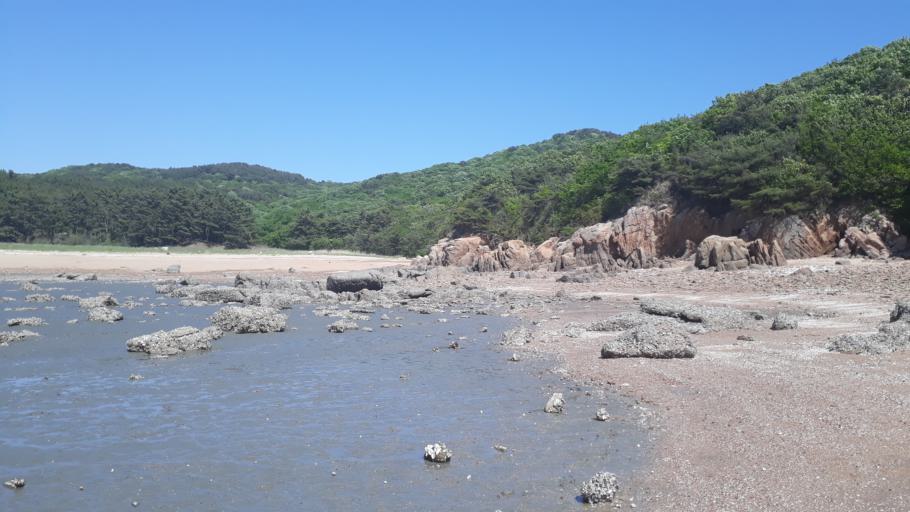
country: KR
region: Incheon
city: Incheon
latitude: 37.4014
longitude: 126.4042
